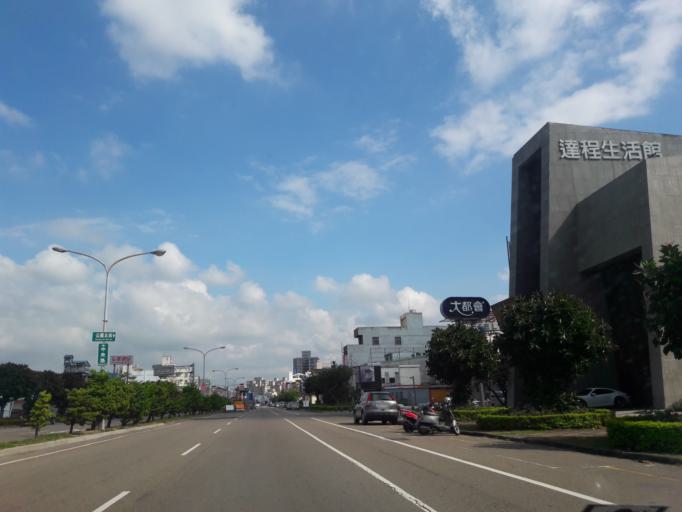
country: TW
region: Taiwan
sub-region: Hsinchu
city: Hsinchu
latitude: 24.6941
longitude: 120.8896
